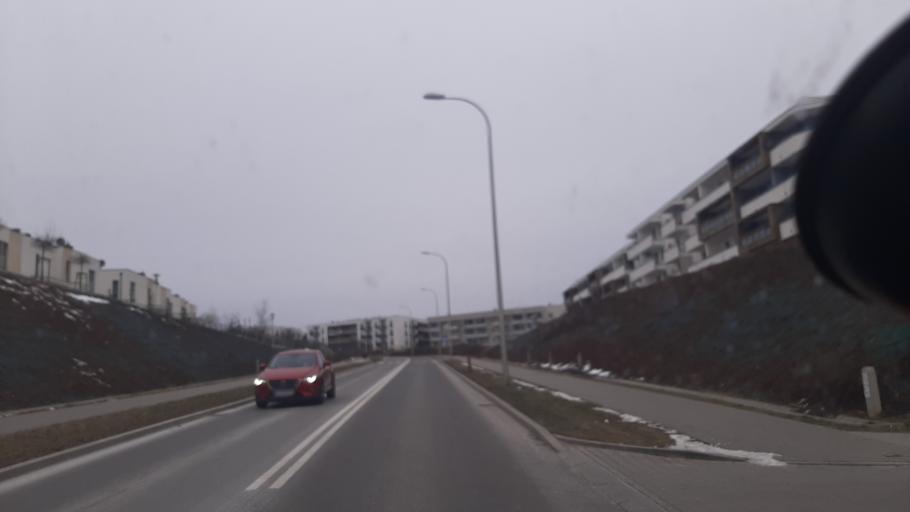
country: PL
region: Lublin Voivodeship
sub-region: Powiat lubelski
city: Lublin
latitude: 51.2710
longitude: 22.5825
